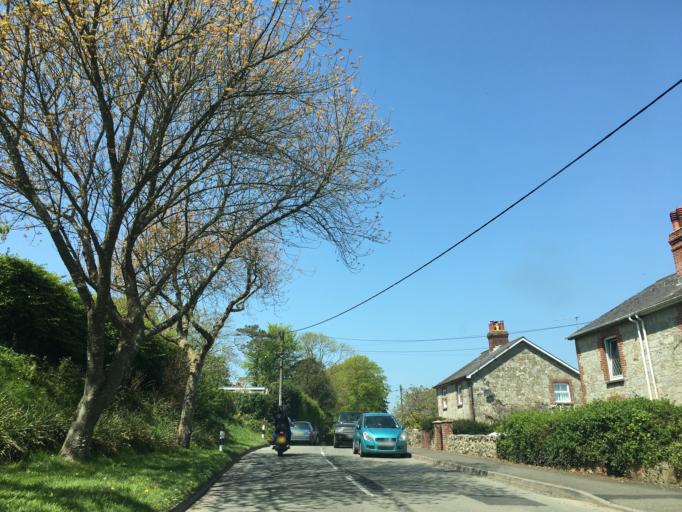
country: GB
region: England
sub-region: Isle of Wight
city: Niton
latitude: 50.5958
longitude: -1.2630
